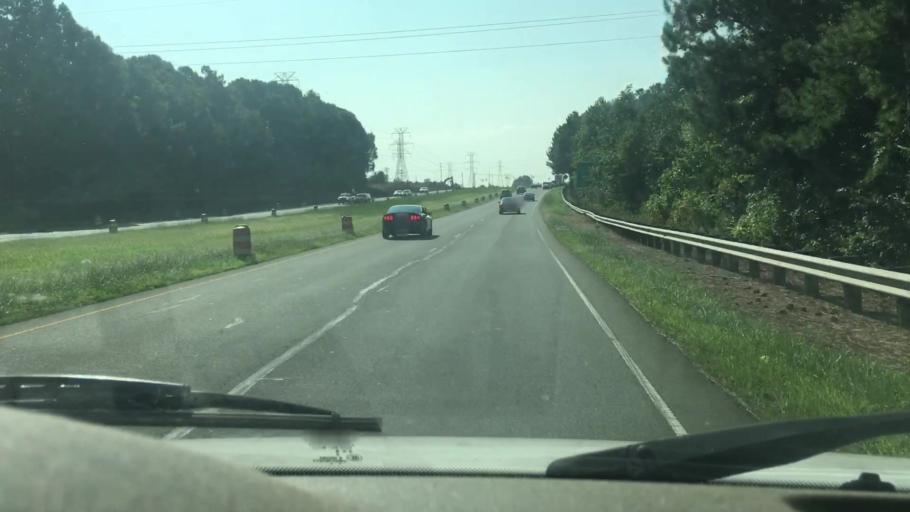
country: US
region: North Carolina
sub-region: Gaston County
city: Mount Holly
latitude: 35.3286
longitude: -80.9493
